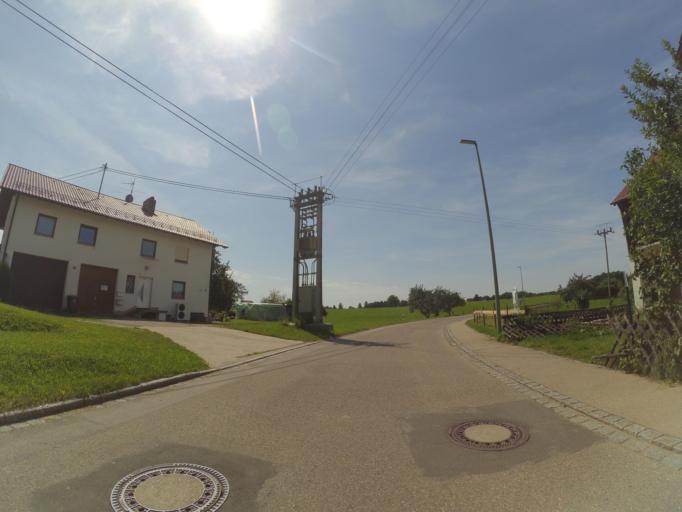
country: DE
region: Bavaria
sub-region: Swabia
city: Unteregg
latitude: 47.9626
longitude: 10.4641
